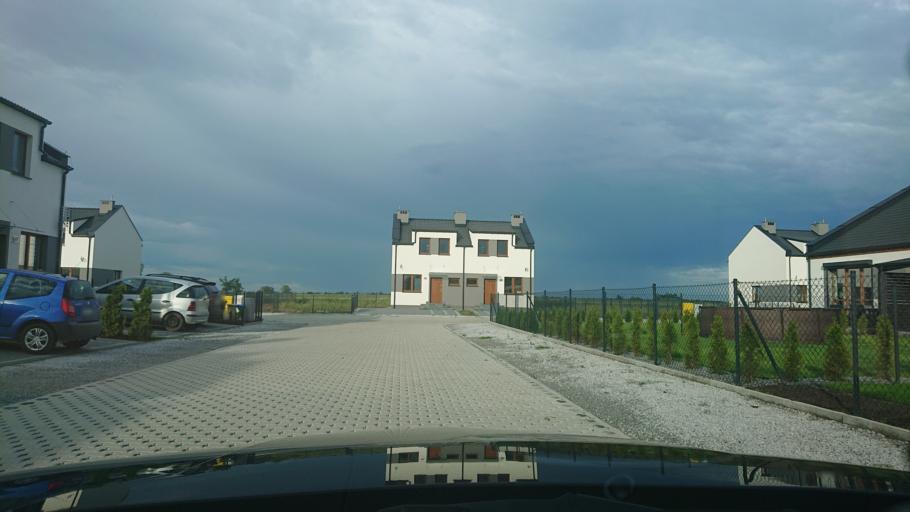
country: PL
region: Greater Poland Voivodeship
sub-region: Powiat gnieznienski
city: Gniezno
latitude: 52.5685
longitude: 17.6161
